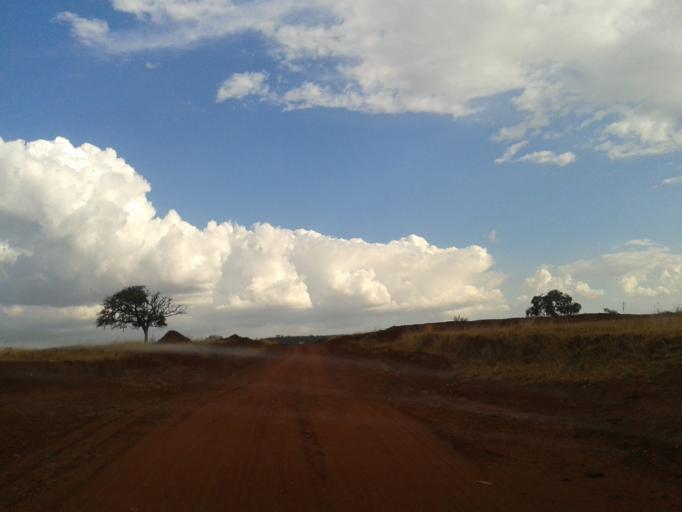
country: BR
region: Minas Gerais
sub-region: Santa Vitoria
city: Santa Vitoria
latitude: -19.1871
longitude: -49.9421
